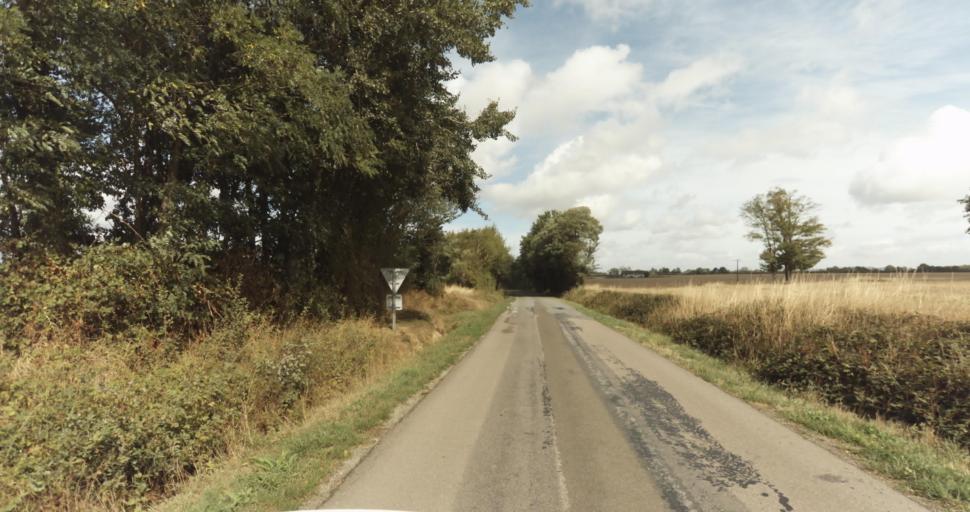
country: FR
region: Lower Normandy
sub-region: Departement de l'Orne
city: Gace
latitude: 48.8005
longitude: 0.3887
